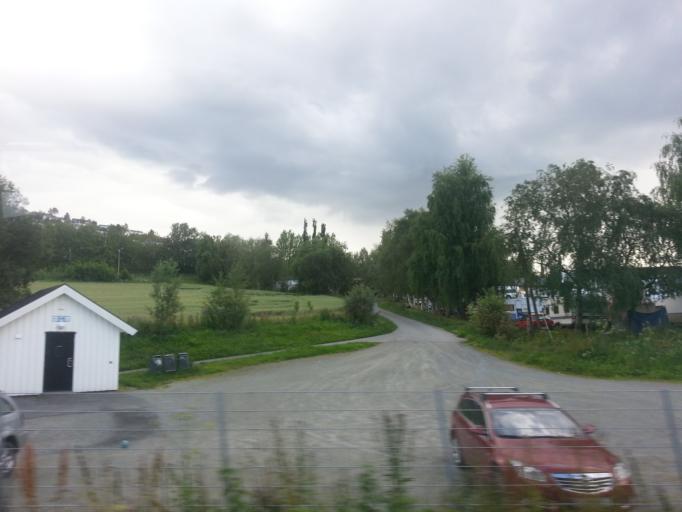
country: NO
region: Sor-Trondelag
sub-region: Malvik
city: Malvik
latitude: 63.4417
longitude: 10.6420
